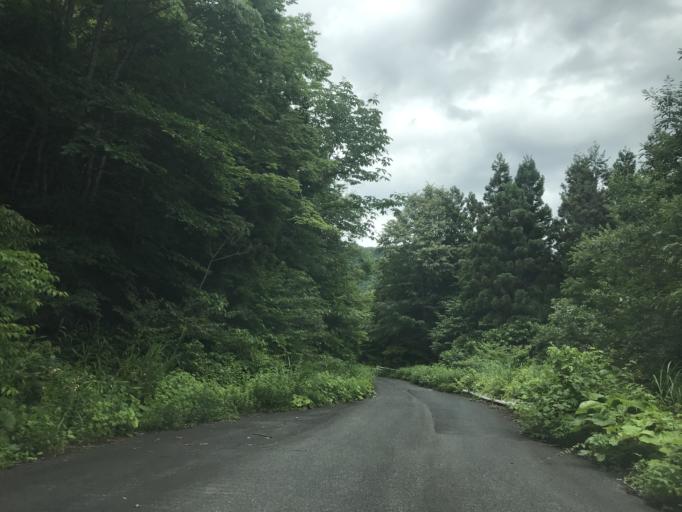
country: JP
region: Iwate
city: Ichinoseki
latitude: 38.9489
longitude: 140.8793
